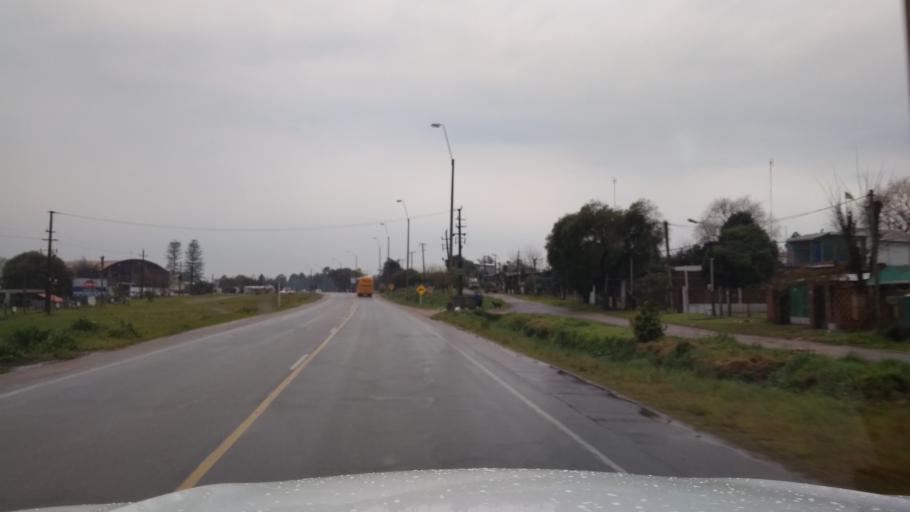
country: UY
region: Canelones
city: Toledo
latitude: -34.7569
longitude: -56.1117
